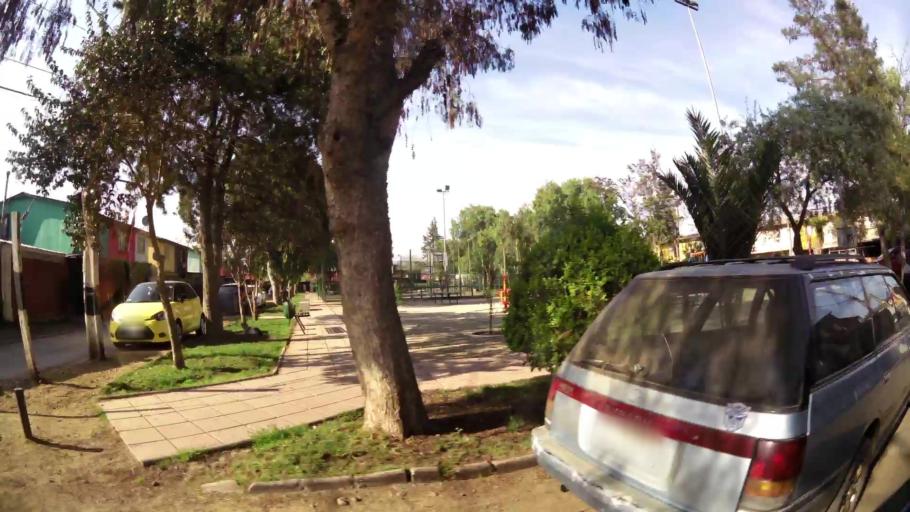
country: CL
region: Santiago Metropolitan
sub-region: Provincia de Talagante
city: Talagante
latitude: -33.6727
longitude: -70.9381
